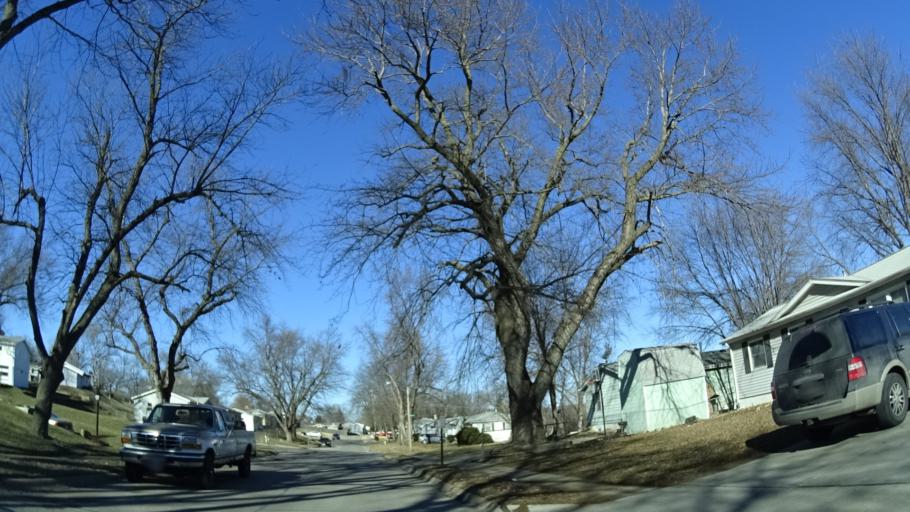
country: US
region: Nebraska
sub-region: Sarpy County
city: Bellevue
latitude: 41.1459
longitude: -95.9085
